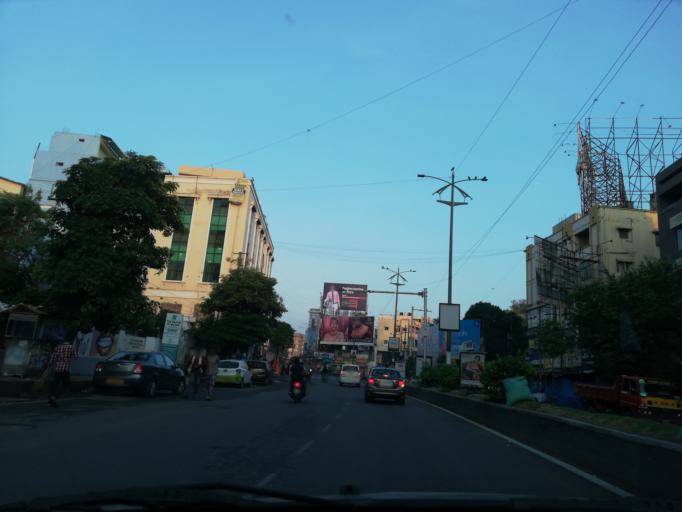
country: IN
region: Telangana
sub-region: Hyderabad
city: Hyderabad
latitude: 17.4006
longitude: 78.4894
